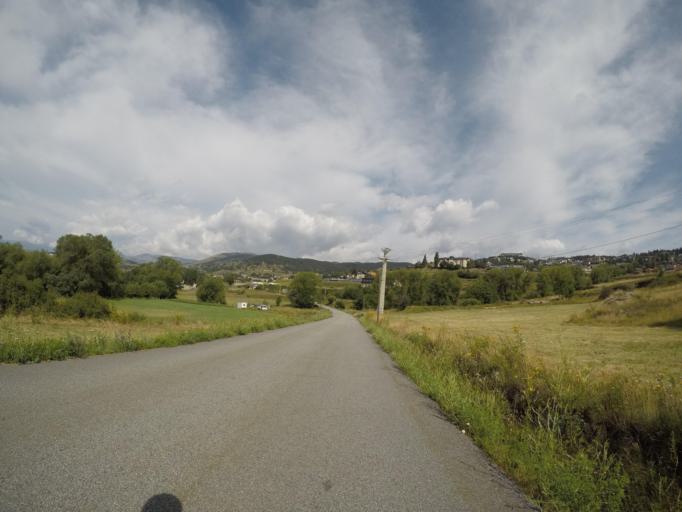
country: ES
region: Catalonia
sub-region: Provincia de Girona
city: Llivia
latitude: 42.4948
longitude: 2.0422
